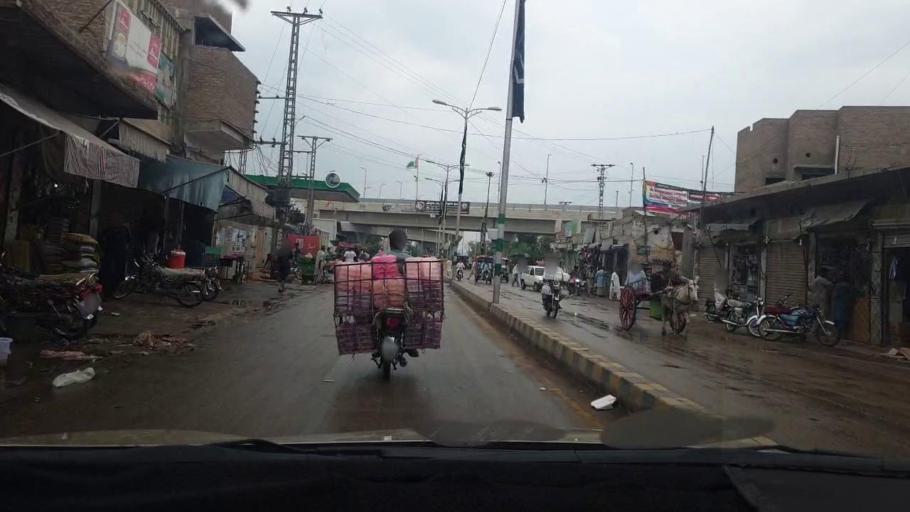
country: PK
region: Sindh
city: Larkana
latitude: 27.5606
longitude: 68.2078
